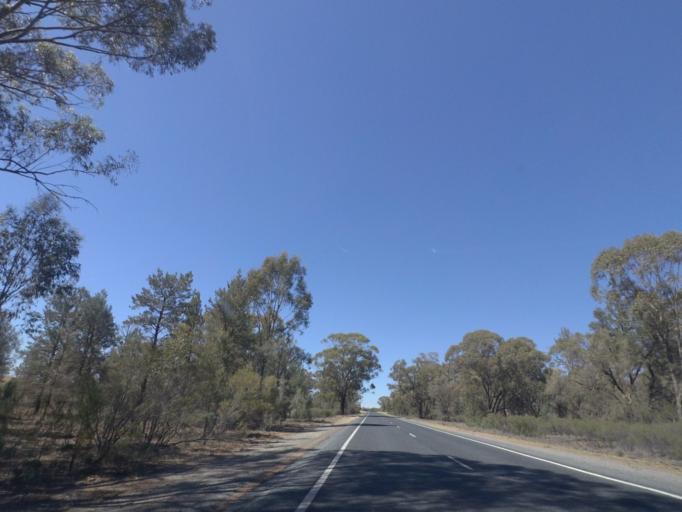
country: AU
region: New South Wales
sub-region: Narrandera
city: Narrandera
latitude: -34.4428
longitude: 146.8408
